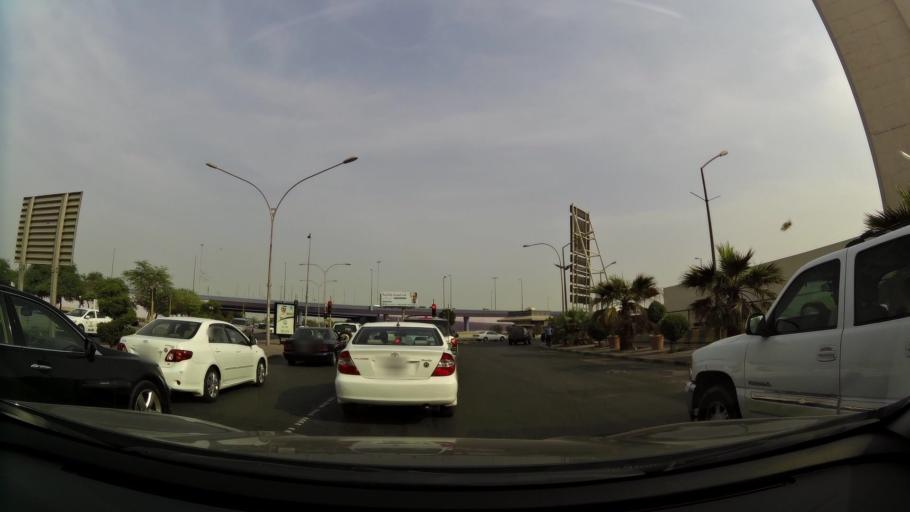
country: KW
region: Al Farwaniyah
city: Janub as Surrah
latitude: 29.2720
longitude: 47.9679
